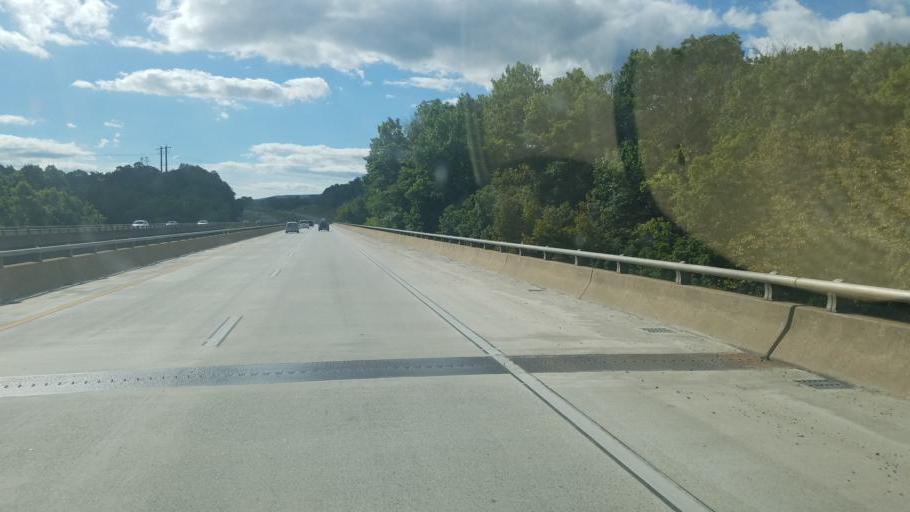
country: US
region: Virginia
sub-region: Warren County
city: Front Royal
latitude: 38.9567
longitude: -78.1867
